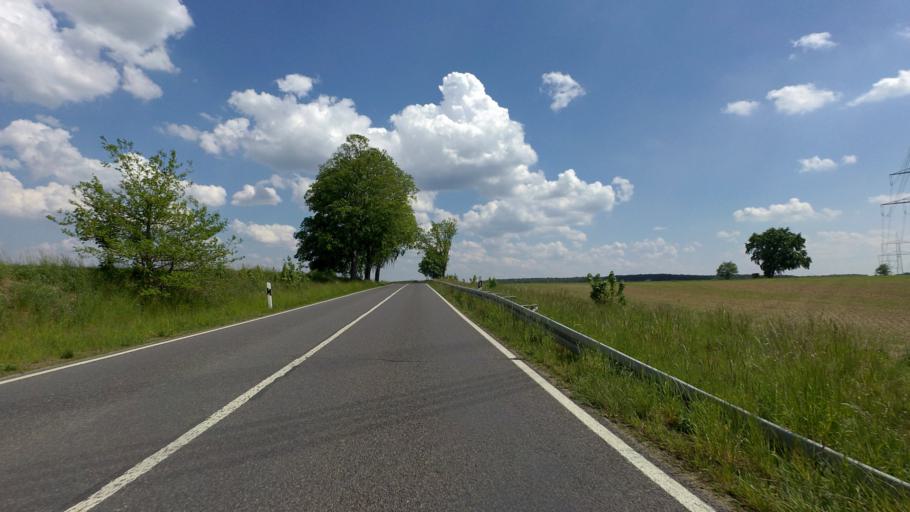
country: DE
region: Brandenburg
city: Straupitz
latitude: 51.9163
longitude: 14.1398
